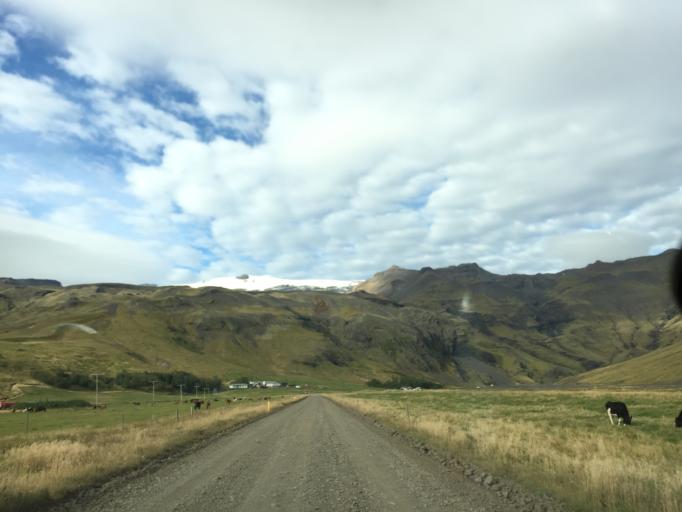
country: IS
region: South
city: Vestmannaeyjar
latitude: 63.5530
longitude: -19.6266
